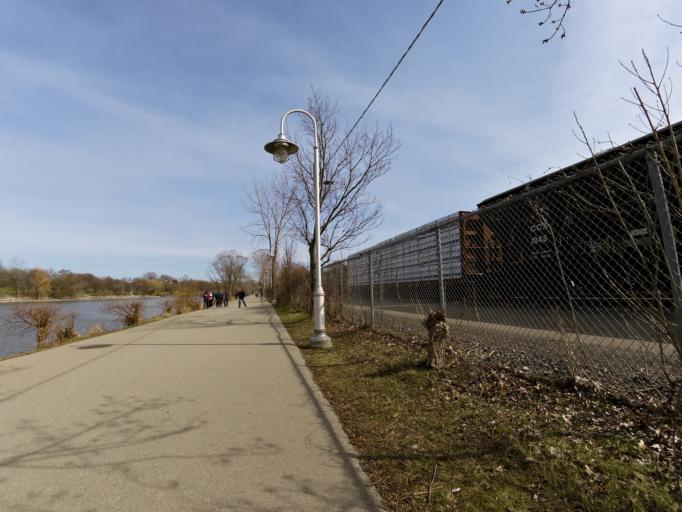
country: CA
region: Ontario
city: Hamilton
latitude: 43.2701
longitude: -79.8759
